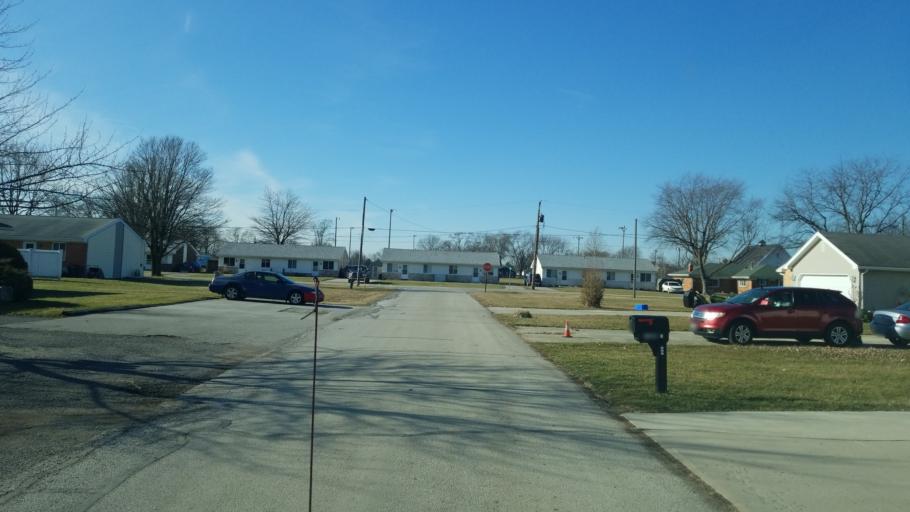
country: US
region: Ohio
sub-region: Wood County
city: Weston
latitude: 41.4086
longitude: -83.8576
